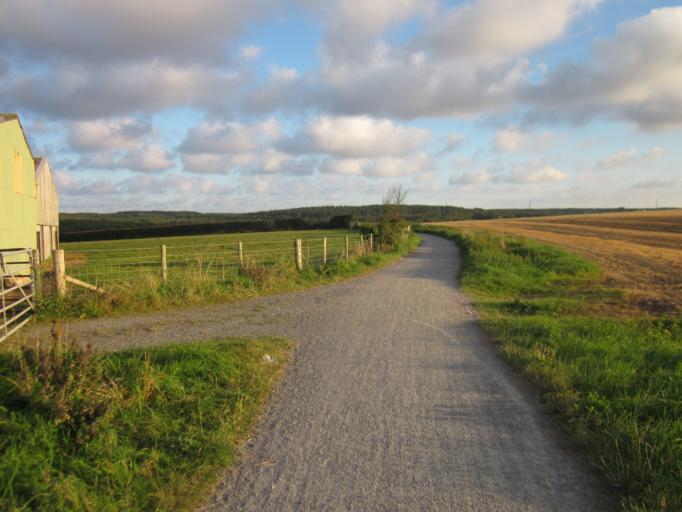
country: GB
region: England
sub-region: Kent
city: Tankerton
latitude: 51.3442
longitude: 1.0478
